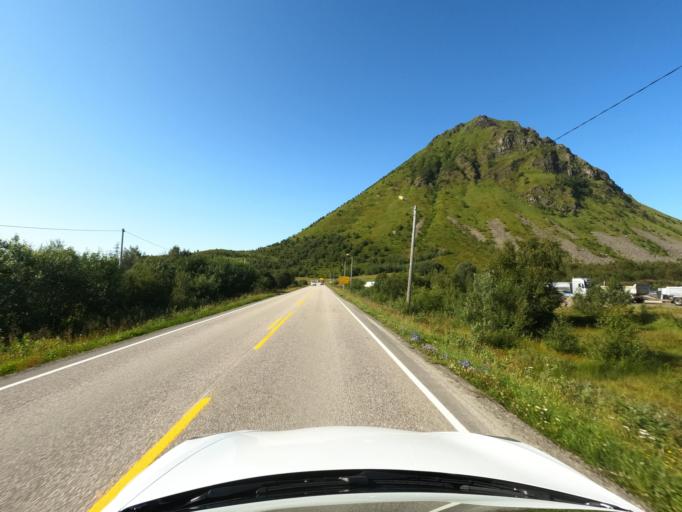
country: NO
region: Nordland
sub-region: Vestvagoy
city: Evjen
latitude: 68.2722
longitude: 13.9701
